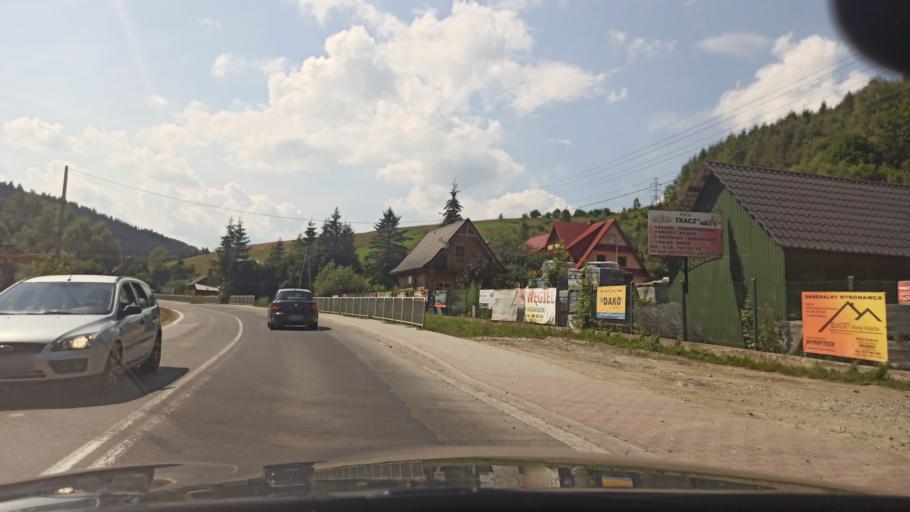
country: PL
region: Lesser Poland Voivodeship
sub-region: Powiat nowotarski
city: Kroscienko nad Dunajcem
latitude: 49.4392
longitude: 20.3860
